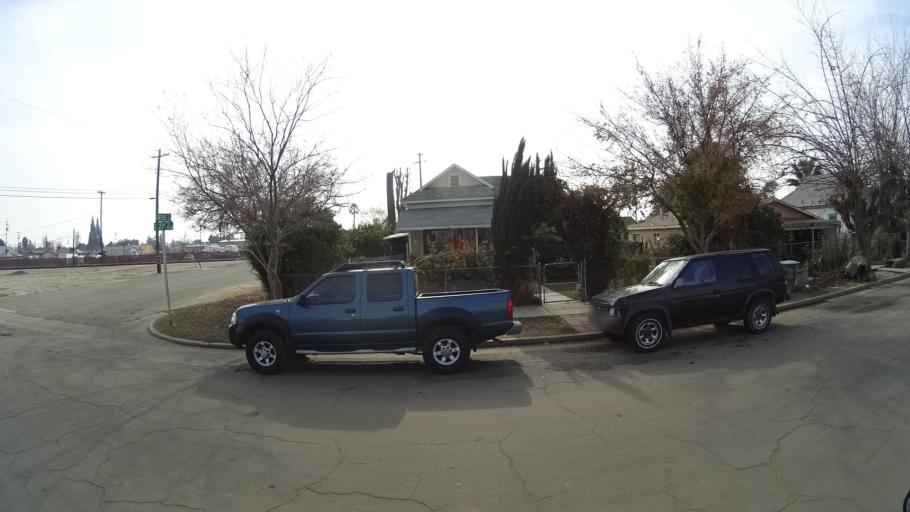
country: US
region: California
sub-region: Kern County
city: Bakersfield
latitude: 35.3748
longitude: -118.9888
